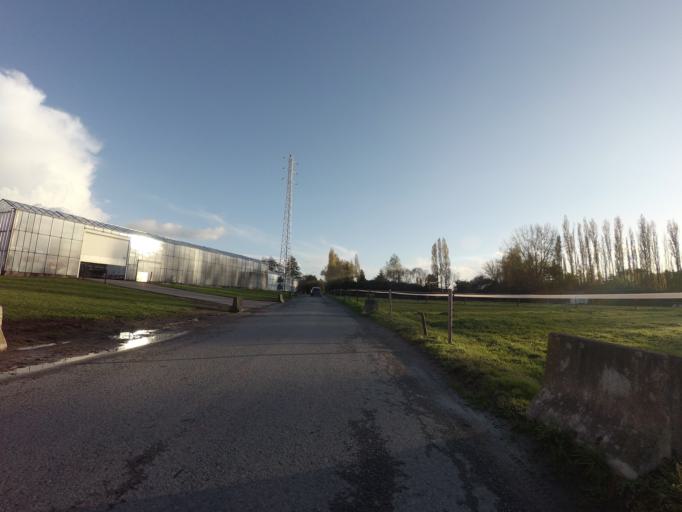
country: BE
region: Flanders
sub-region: Provincie Antwerpen
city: Schelle
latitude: 51.1133
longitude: 4.3538
